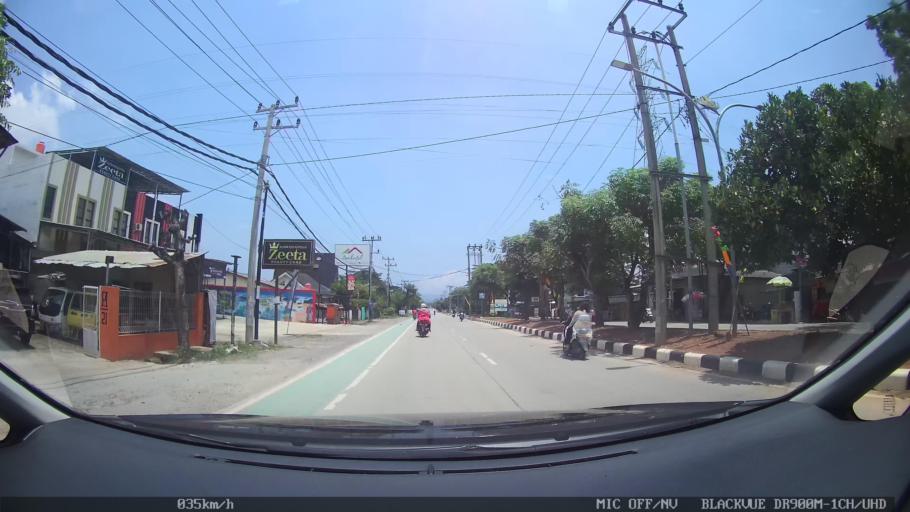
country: ID
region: Lampung
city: Kedaton
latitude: -5.3622
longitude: 105.3036
